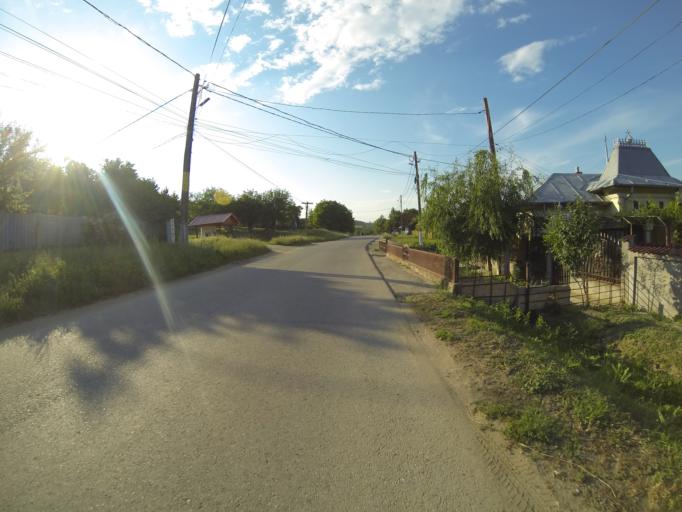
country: RO
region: Dolj
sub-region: Comuna Tuglui
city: Tuglui
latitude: 44.2064
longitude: 23.7967
